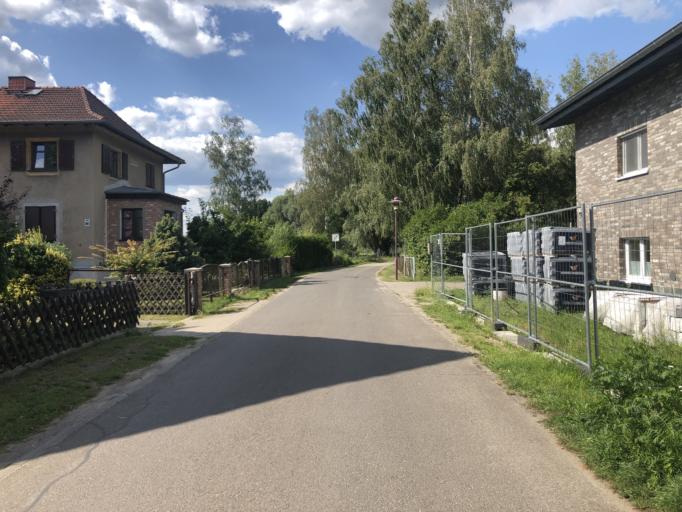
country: DE
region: Brandenburg
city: Mullrose
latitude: 52.2493
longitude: 14.4108
